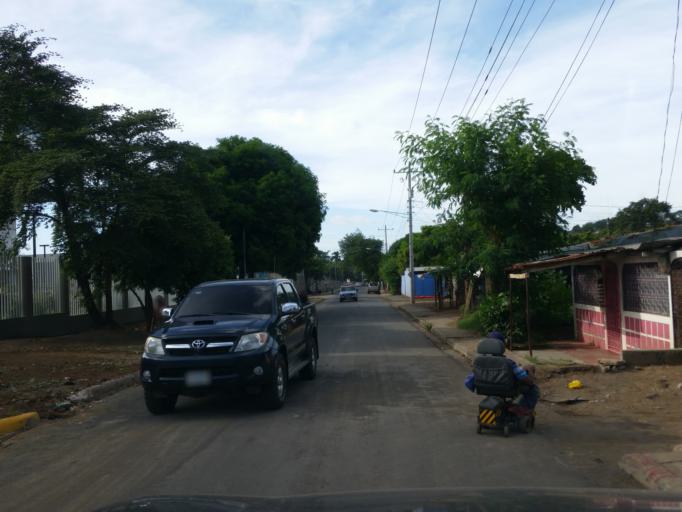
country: NI
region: Managua
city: Managua
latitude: 12.1328
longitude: -86.2779
